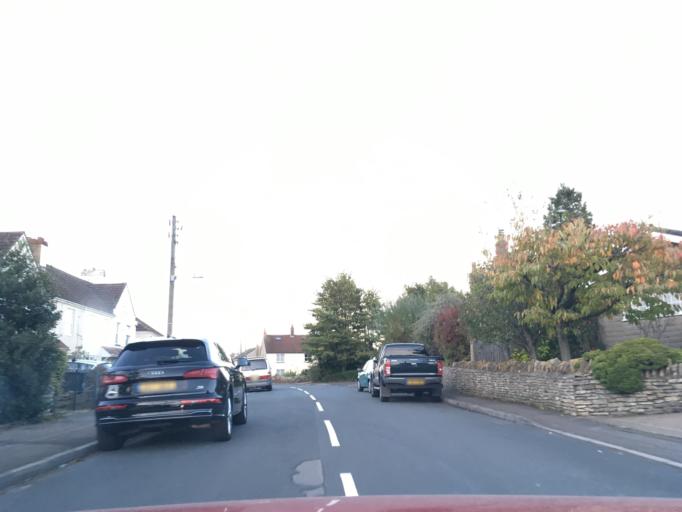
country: GB
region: England
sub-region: South Gloucestershire
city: Stoke Gifford
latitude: 51.5194
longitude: -2.5390
